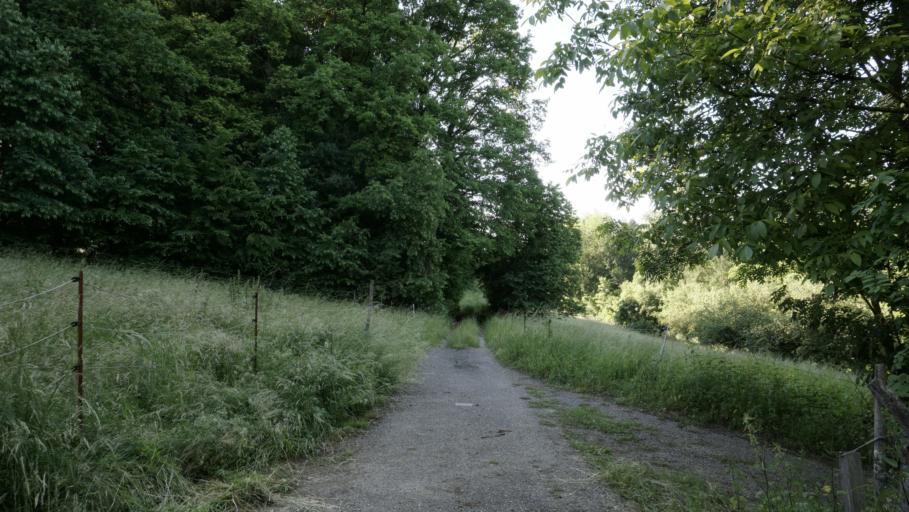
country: DE
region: Baden-Wuerttemberg
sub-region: Karlsruhe Region
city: Billigheim
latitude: 49.3797
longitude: 9.2094
